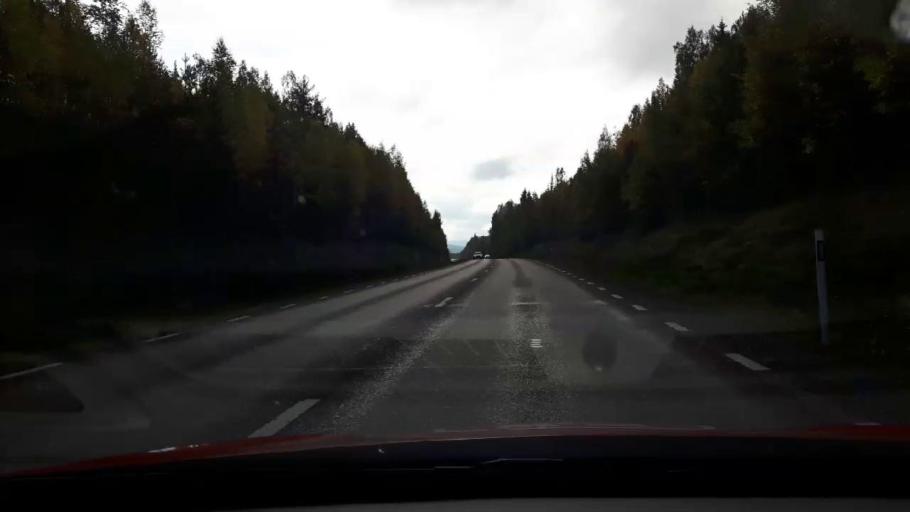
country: SE
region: Gaevleborg
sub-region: Ljusdals Kommun
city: Jaervsoe
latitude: 61.7394
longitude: 16.1596
